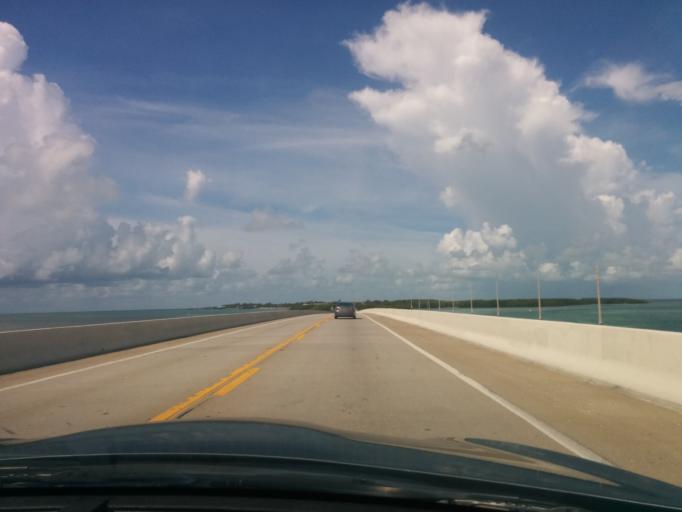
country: US
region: Florida
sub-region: Monroe County
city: Islamorada
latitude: 24.8870
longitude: -80.6812
